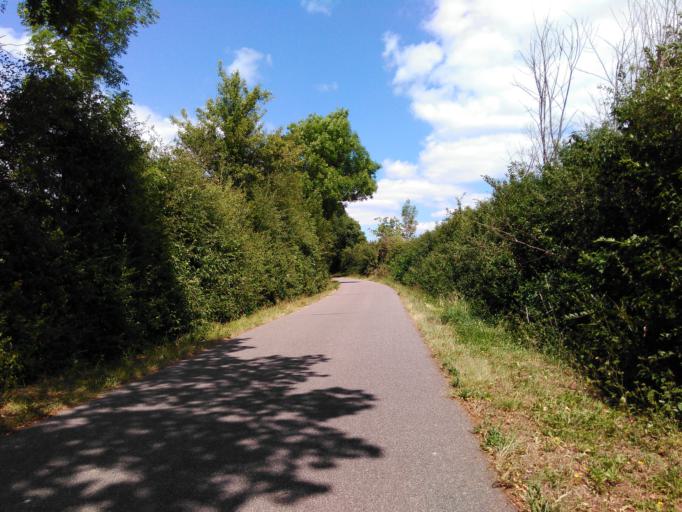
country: LU
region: Luxembourg
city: Hautcharage
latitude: 49.5785
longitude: 5.9030
